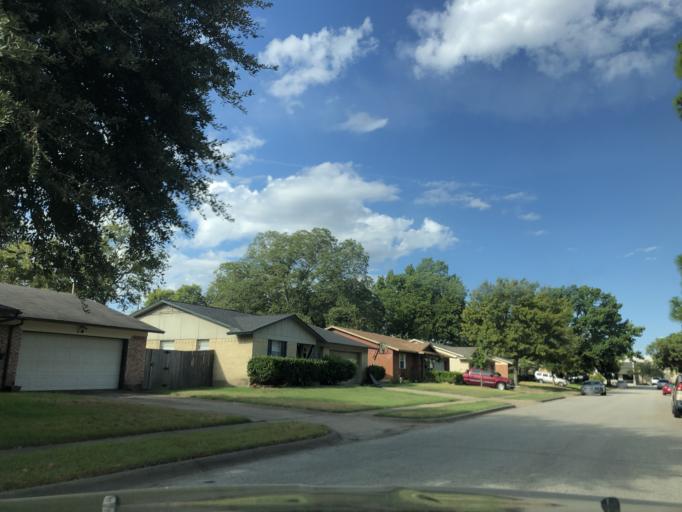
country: US
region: Texas
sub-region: Dallas County
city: Garland
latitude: 32.8845
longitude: -96.6639
